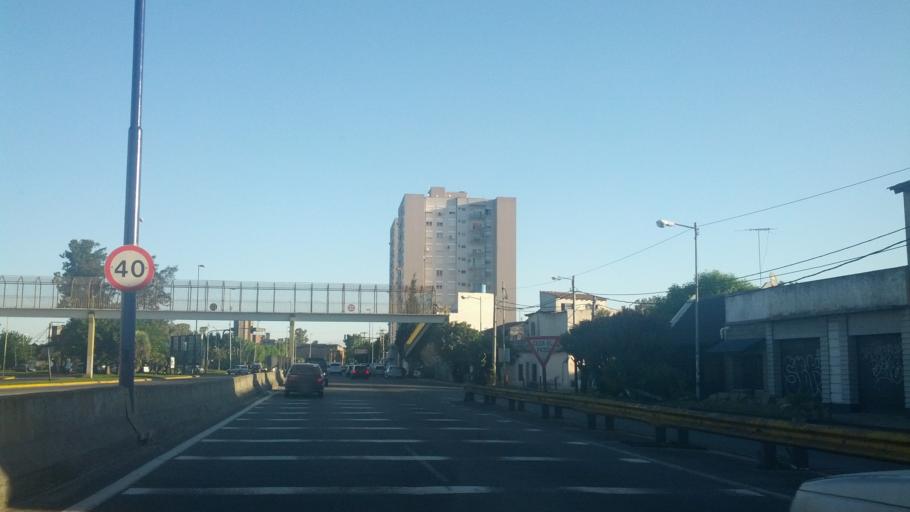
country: AR
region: Buenos Aires
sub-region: Partido de Lomas de Zamora
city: Lomas de Zamora
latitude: -34.7587
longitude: -58.4317
